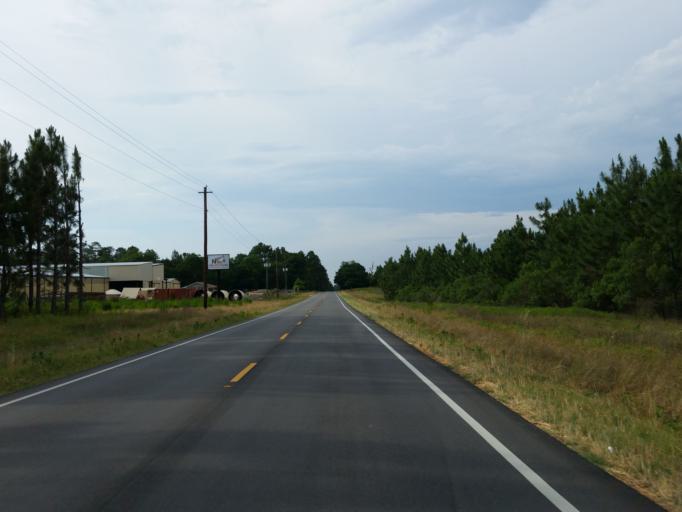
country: US
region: Georgia
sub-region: Turner County
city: Ashburn
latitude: 31.7293
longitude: -83.6656
